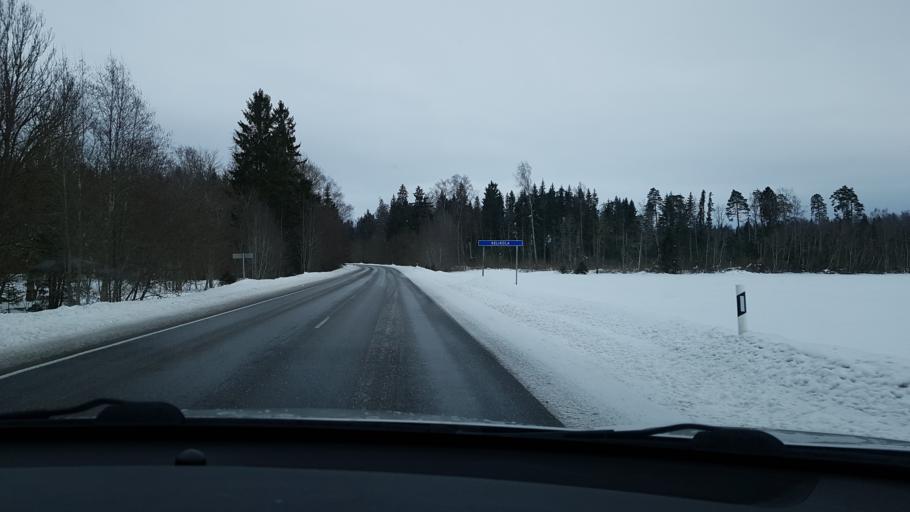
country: EE
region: Jaervamaa
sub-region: Jaerva-Jaani vald
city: Jarva-Jaani
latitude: 59.0993
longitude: 25.8177
